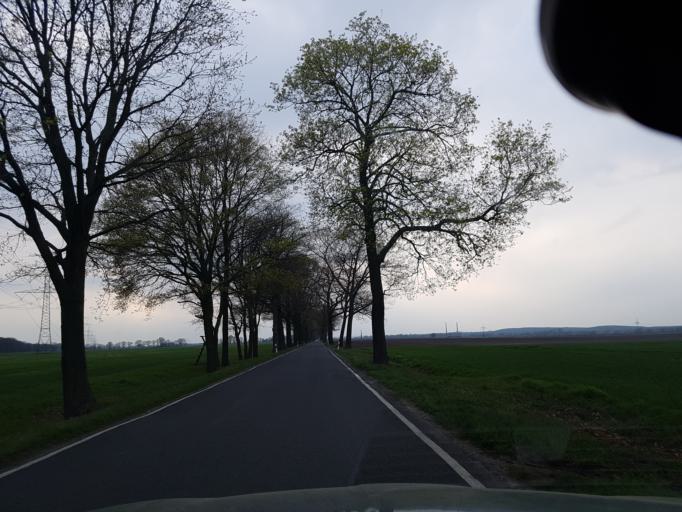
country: DE
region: Brandenburg
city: Schraden
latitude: 51.4502
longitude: 13.6692
